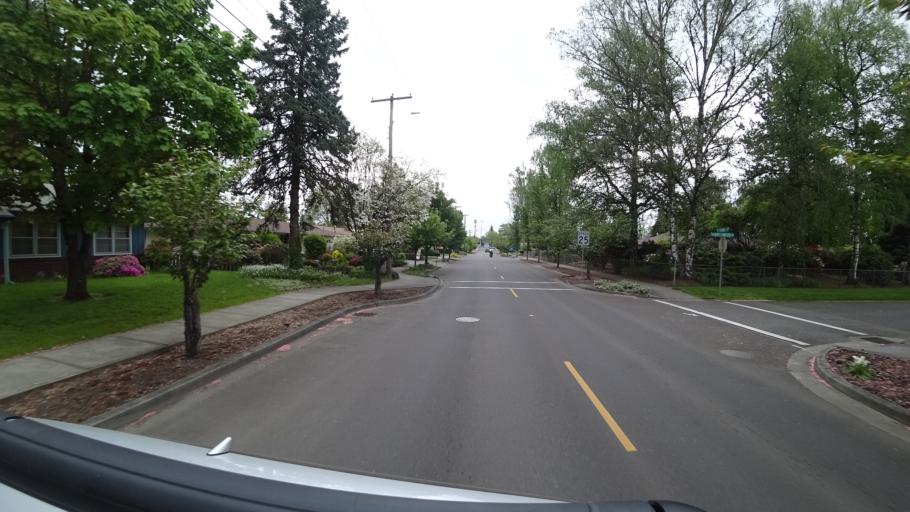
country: US
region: Oregon
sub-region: Washington County
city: Hillsboro
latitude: 45.5283
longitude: -122.9773
